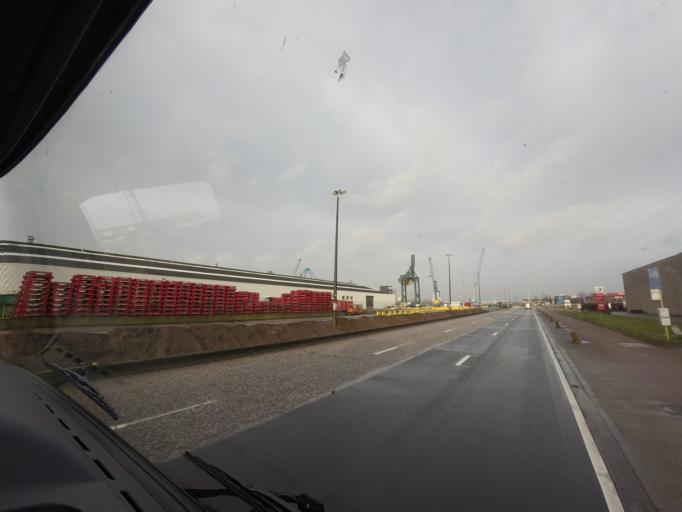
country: BE
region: Flanders
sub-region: Provincie Antwerpen
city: Stabroek
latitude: 51.3230
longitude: 4.3468
